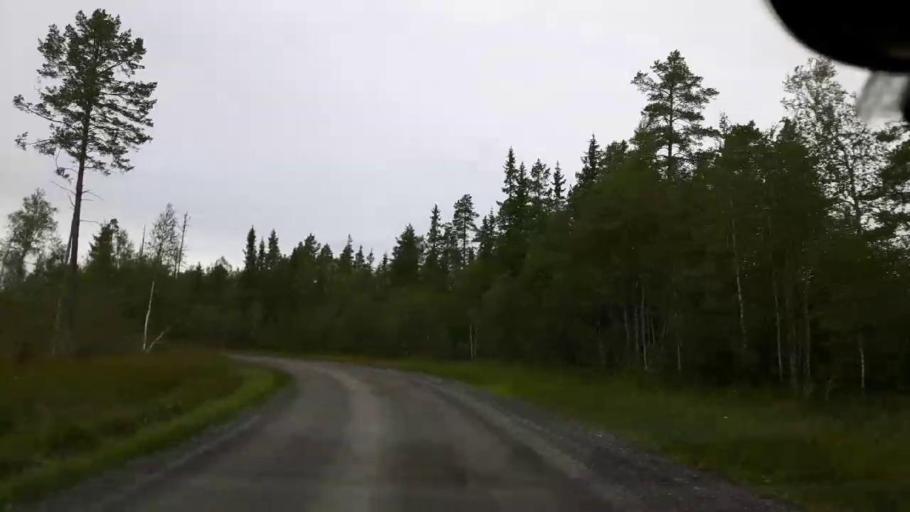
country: SE
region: Jaemtland
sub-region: Krokoms Kommun
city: Krokom
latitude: 63.2887
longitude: 14.3826
